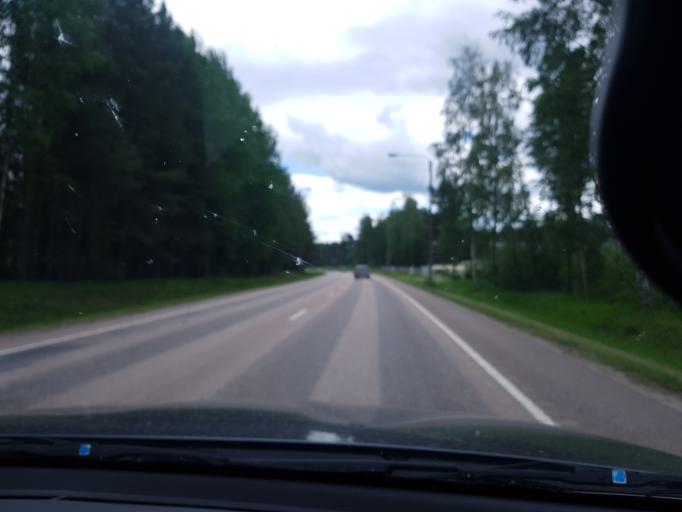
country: FI
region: Pirkanmaa
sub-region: Tampere
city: Paelkaene
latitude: 61.3570
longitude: 24.2459
